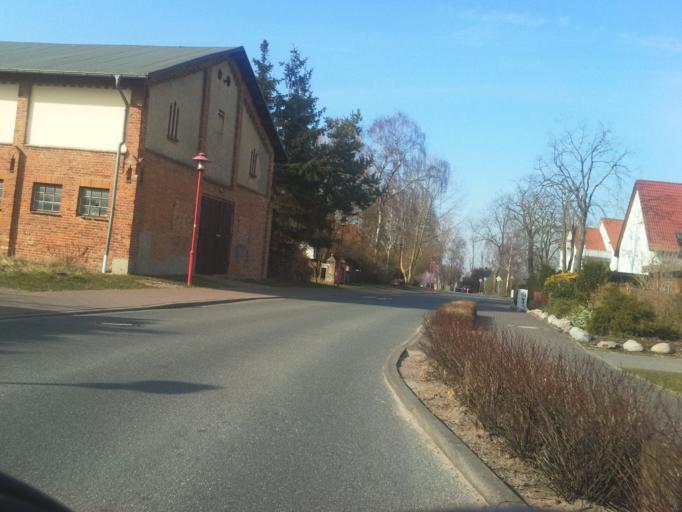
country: DE
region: Mecklenburg-Vorpommern
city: Lambrechtshagen
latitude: 54.1131
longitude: 12.0356
